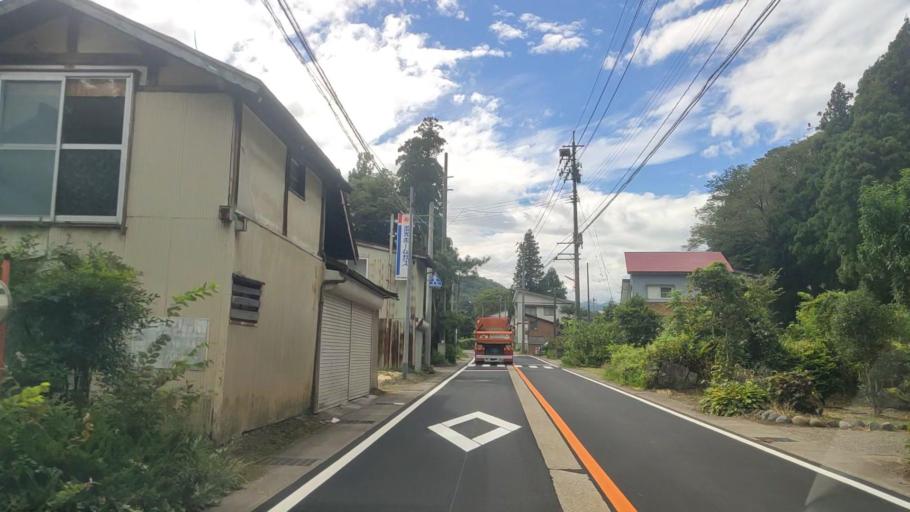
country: JP
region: Niigata
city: Arai
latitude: 36.9585
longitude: 138.2706
